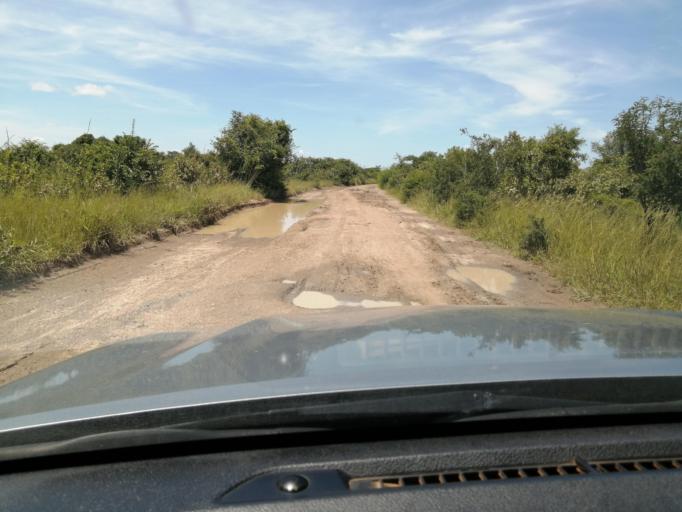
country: ZM
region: Central
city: Chibombo
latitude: -15.0574
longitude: 27.8286
